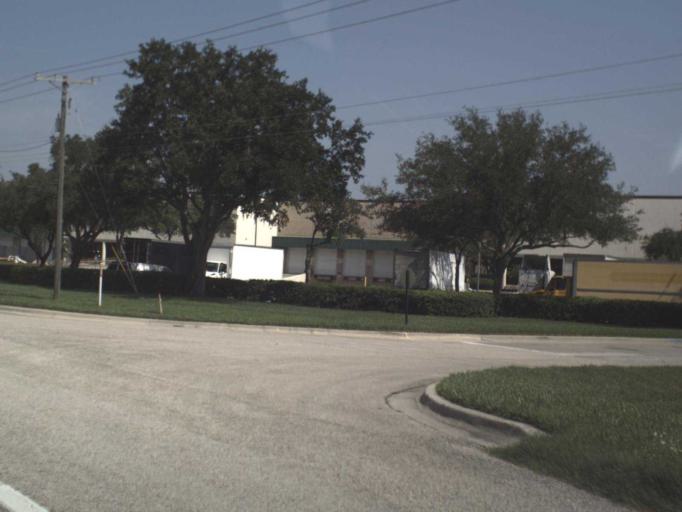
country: US
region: Florida
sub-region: Hillsborough County
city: Palm River-Clair Mel
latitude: 27.9514
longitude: -82.3631
